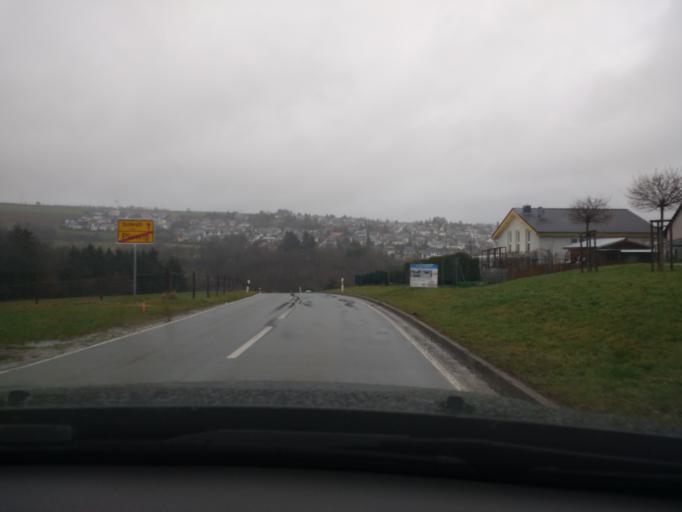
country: DE
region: Rheinland-Pfalz
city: Pluwig
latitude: 49.6923
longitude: 6.7125
